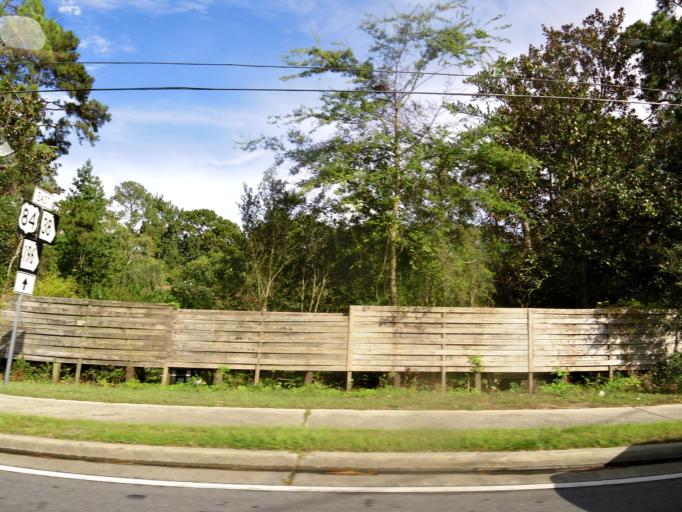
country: US
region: Georgia
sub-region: Liberty County
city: Hinesville
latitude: 31.8379
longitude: -81.5953
